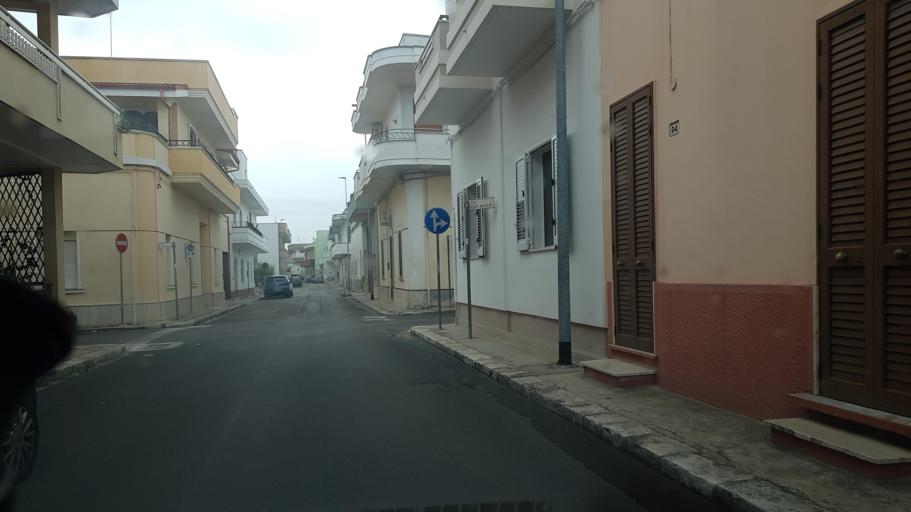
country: IT
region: Apulia
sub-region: Provincia di Lecce
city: Leverano
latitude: 40.2865
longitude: 17.9920
